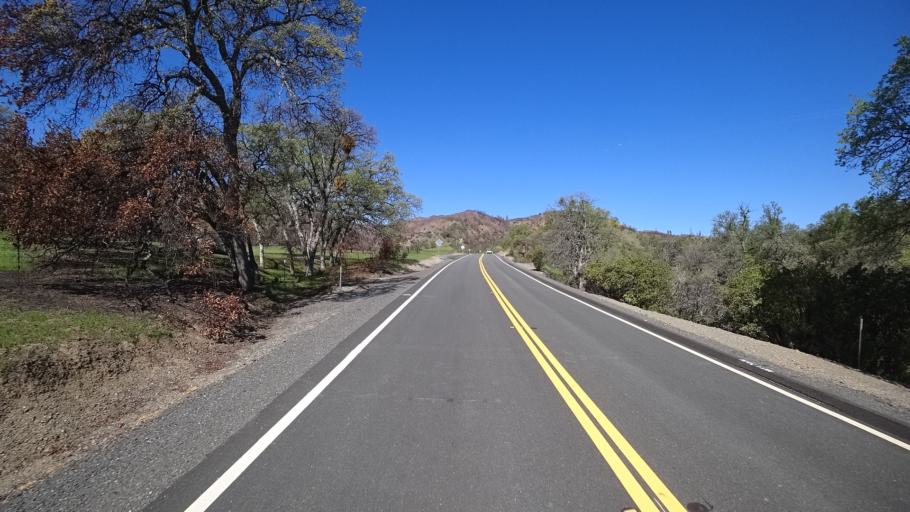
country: US
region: California
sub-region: Glenn County
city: Orland
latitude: 39.6552
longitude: -122.5887
